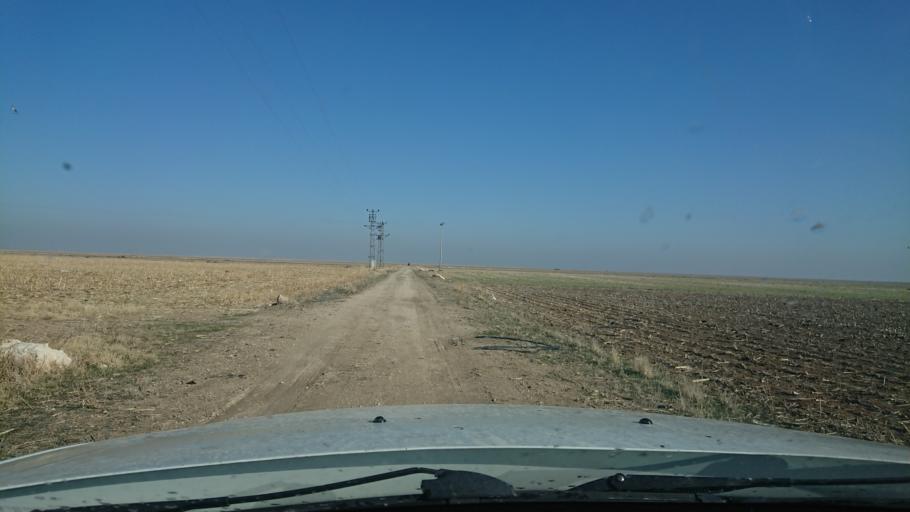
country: TR
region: Aksaray
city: Sultanhani
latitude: 38.3104
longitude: 33.5222
